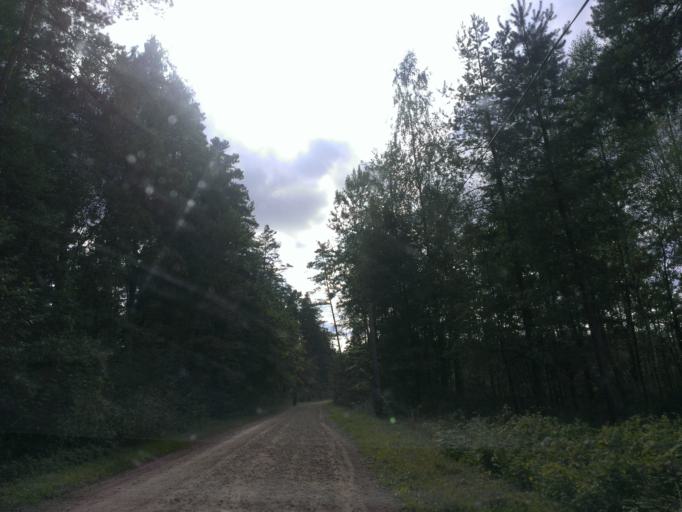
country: LV
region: Incukalns
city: Vangazi
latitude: 57.1158
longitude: 24.5496
